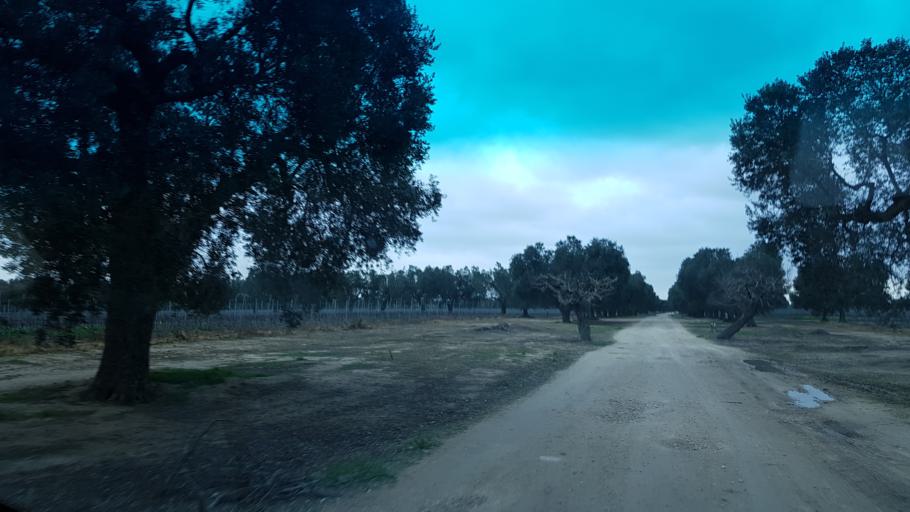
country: IT
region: Apulia
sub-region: Provincia di Brindisi
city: La Rosa
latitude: 40.5910
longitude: 17.9810
